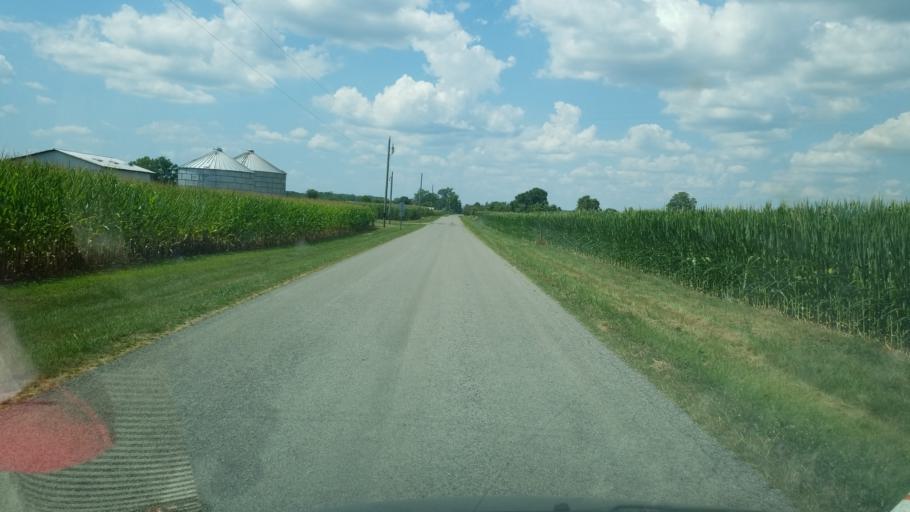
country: US
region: Ohio
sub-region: Champaign County
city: North Lewisburg
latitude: 40.2120
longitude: -83.4865
